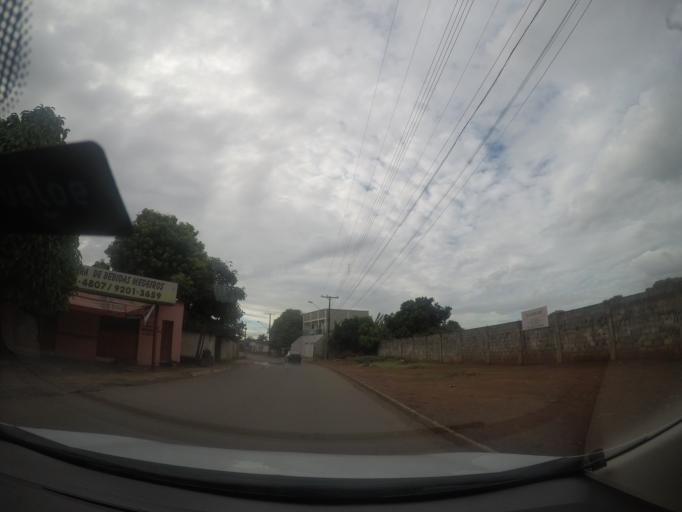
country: BR
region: Goias
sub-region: Goiania
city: Goiania
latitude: -16.6205
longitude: -49.3285
